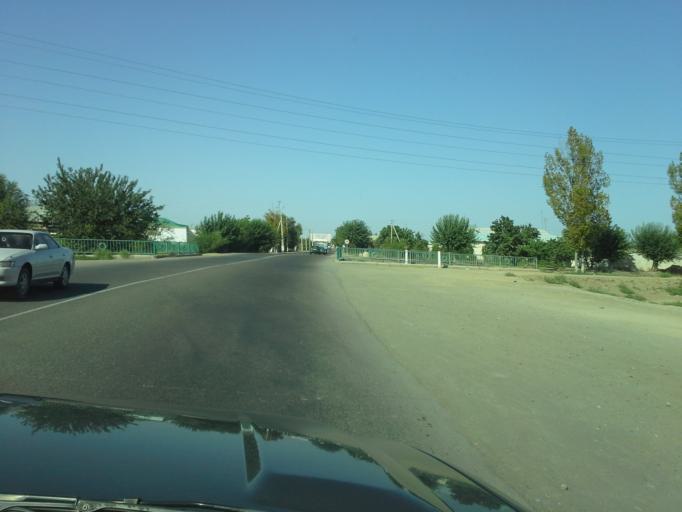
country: TM
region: Dasoguz
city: Dasoguz
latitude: 41.8198
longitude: 59.9522
